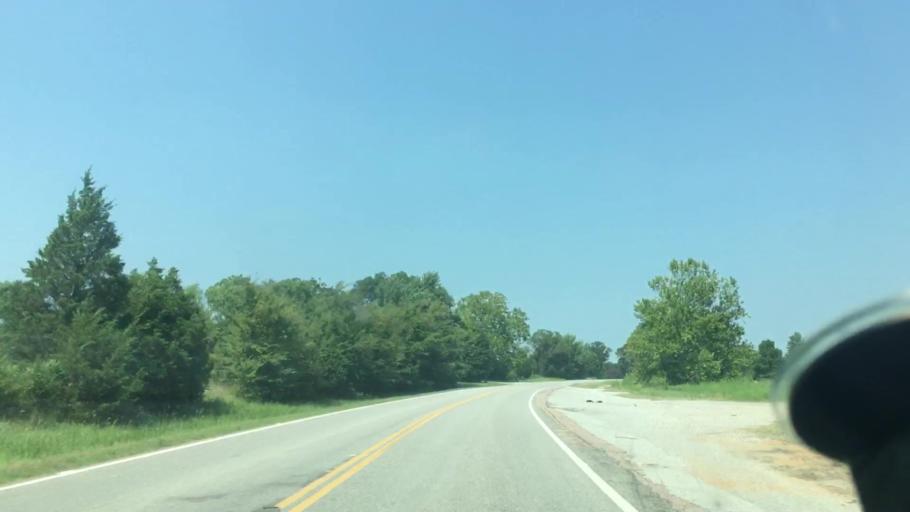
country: US
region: Oklahoma
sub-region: Atoka County
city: Atoka
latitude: 34.2805
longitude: -95.9496
